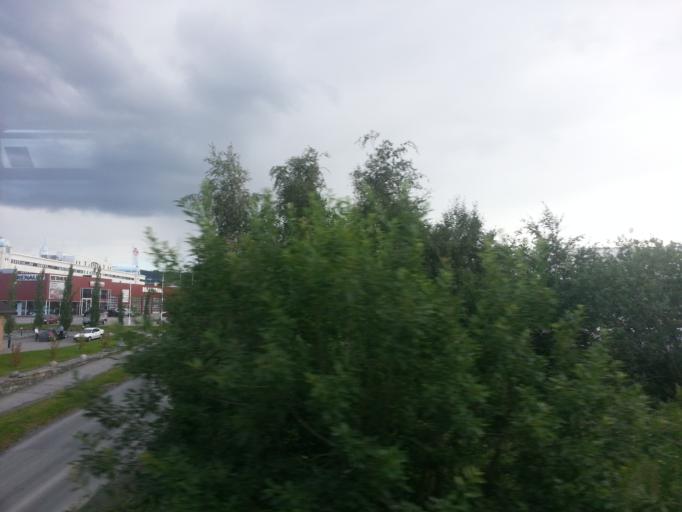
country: NO
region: Sor-Trondelag
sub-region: Trondheim
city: Trondheim
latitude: 63.4362
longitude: 10.4692
